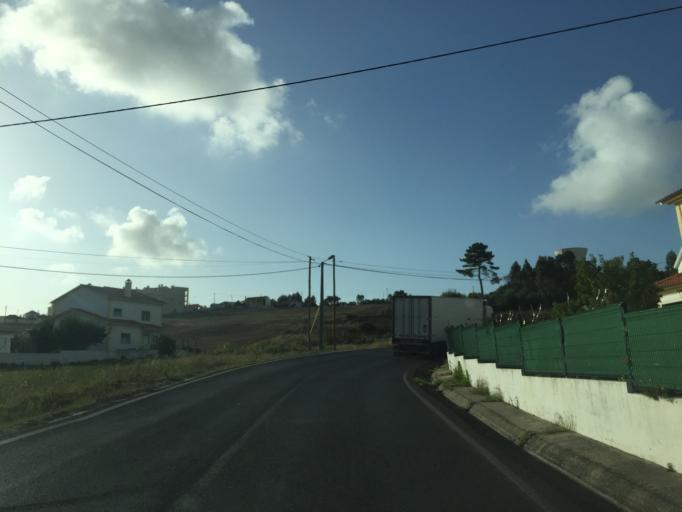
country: PT
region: Lisbon
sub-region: Torres Vedras
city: Torres Vedras
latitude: 39.1087
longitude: -9.2625
